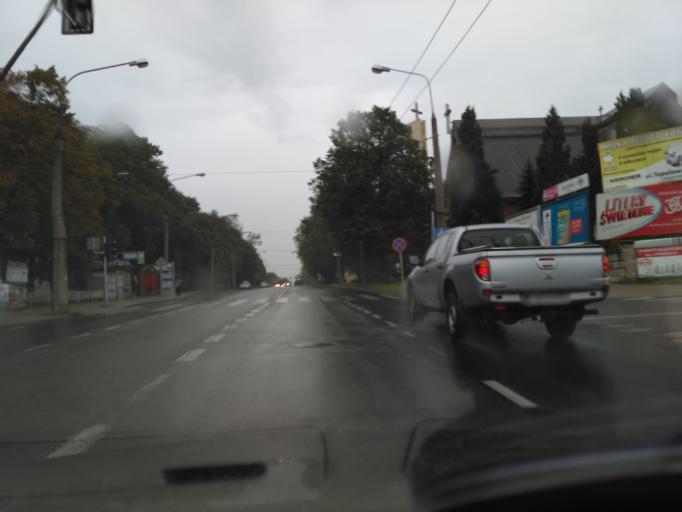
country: PL
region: Lublin Voivodeship
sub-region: Powiat lubelski
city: Lublin
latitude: 51.2332
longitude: 22.5861
